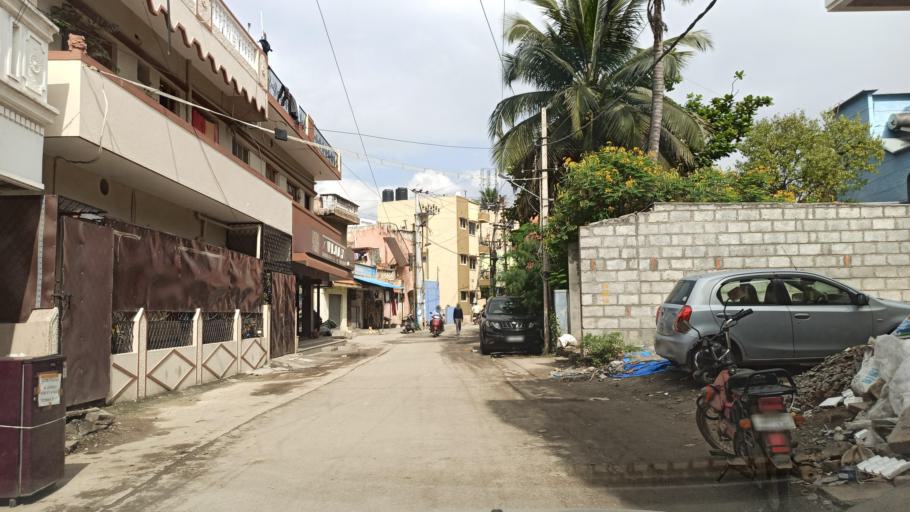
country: IN
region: Karnataka
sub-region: Bangalore Urban
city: Bangalore
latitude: 13.0070
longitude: 77.6743
